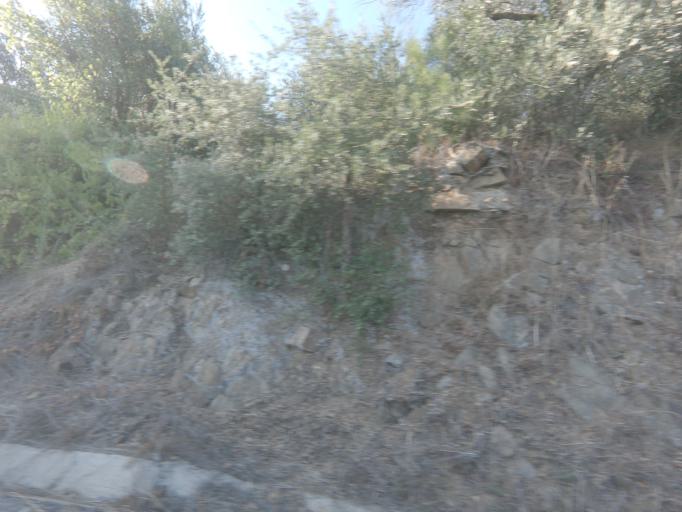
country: PT
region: Vila Real
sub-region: Sabrosa
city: Sabrosa
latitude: 41.2677
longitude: -7.5438
